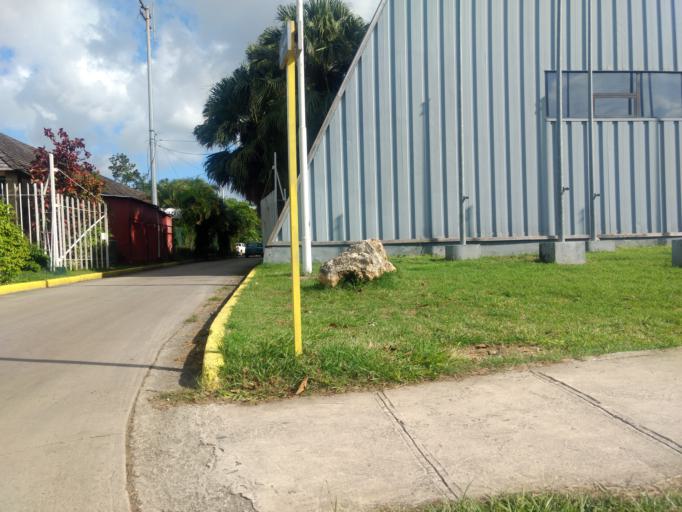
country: CU
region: La Habana
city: Cerro
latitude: 23.0860
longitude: -82.4628
